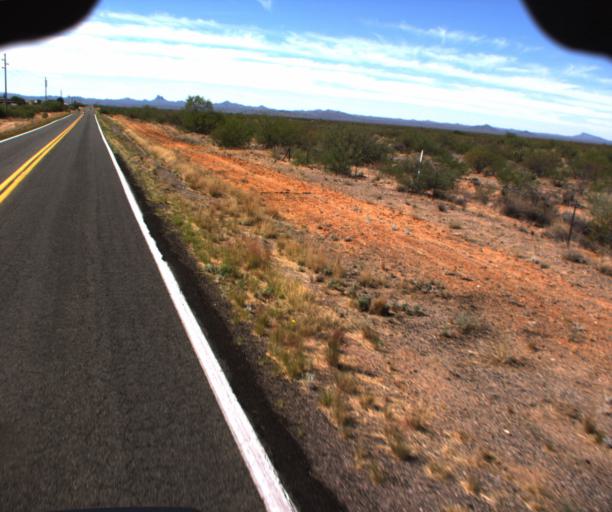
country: US
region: Arizona
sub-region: Yavapai County
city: Congress
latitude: 34.1097
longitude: -112.8329
